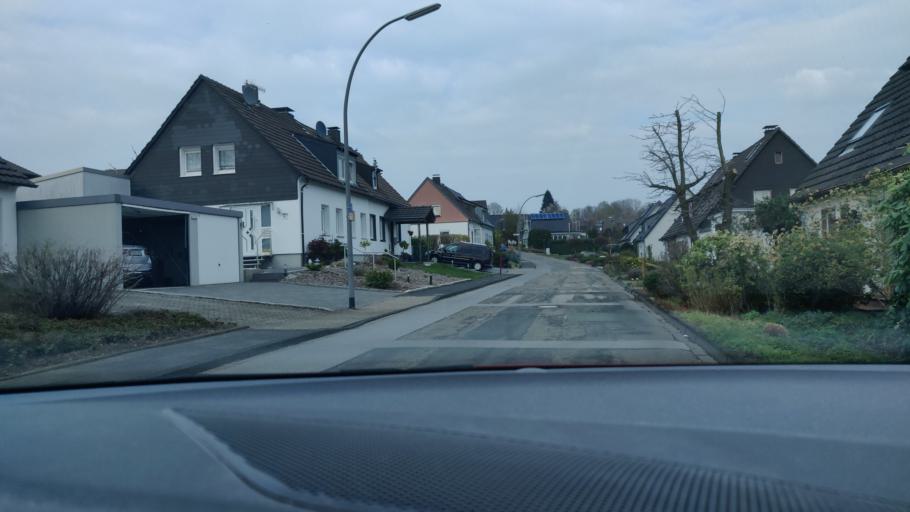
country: DE
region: North Rhine-Westphalia
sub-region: Regierungsbezirk Dusseldorf
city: Velbert
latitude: 51.3263
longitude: 7.0249
